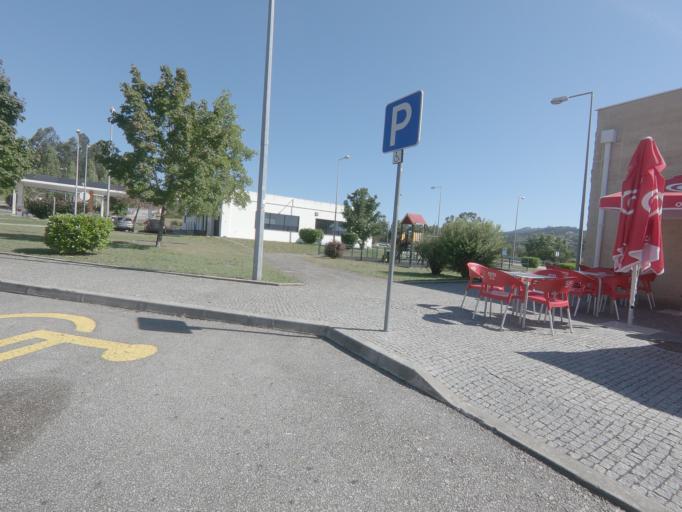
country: PT
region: Porto
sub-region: Marco de Canaveses
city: Marco de Canavezes
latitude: 41.2326
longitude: -8.1788
